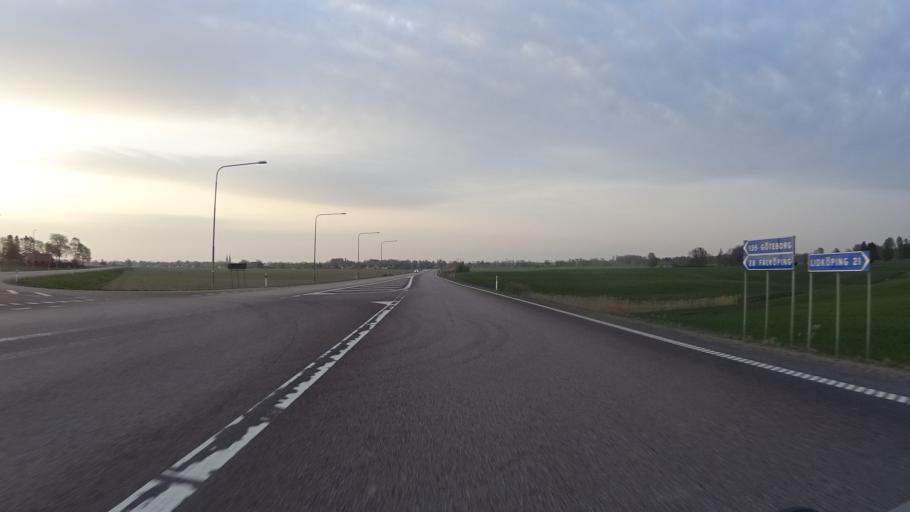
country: SE
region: Vaestra Goetaland
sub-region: Skara Kommun
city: Skara
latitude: 58.3987
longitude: 13.3998
